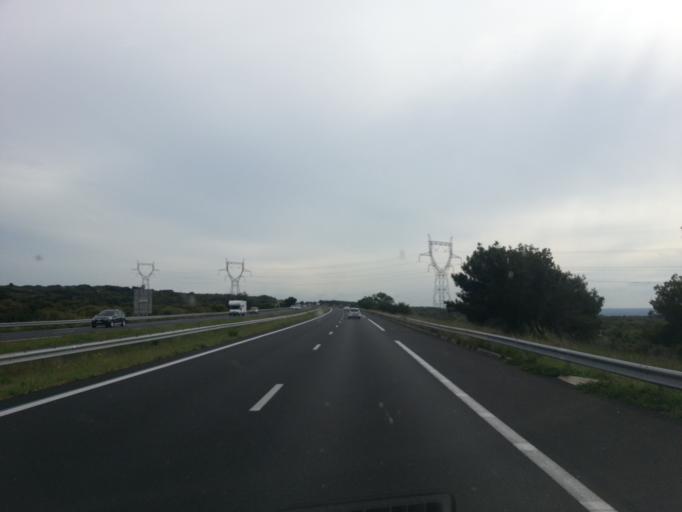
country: FR
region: Languedoc-Roussillon
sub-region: Departement du Gard
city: Saze
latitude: 43.9593
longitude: 4.6303
